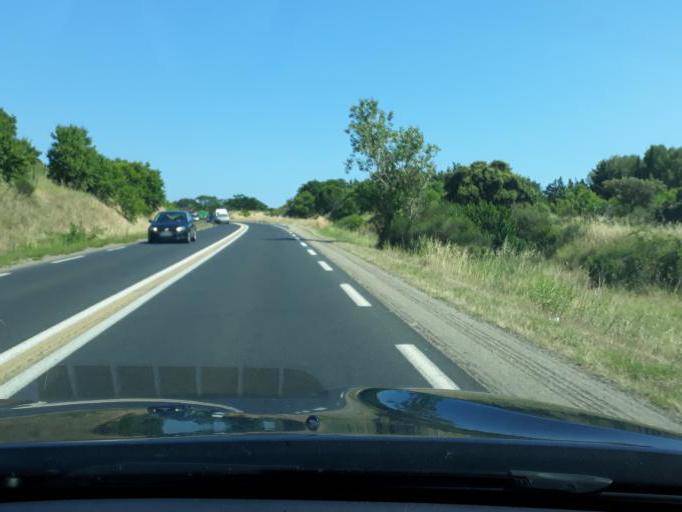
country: FR
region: Languedoc-Roussillon
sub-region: Departement de l'Herault
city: Agde
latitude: 43.2955
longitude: 3.4904
